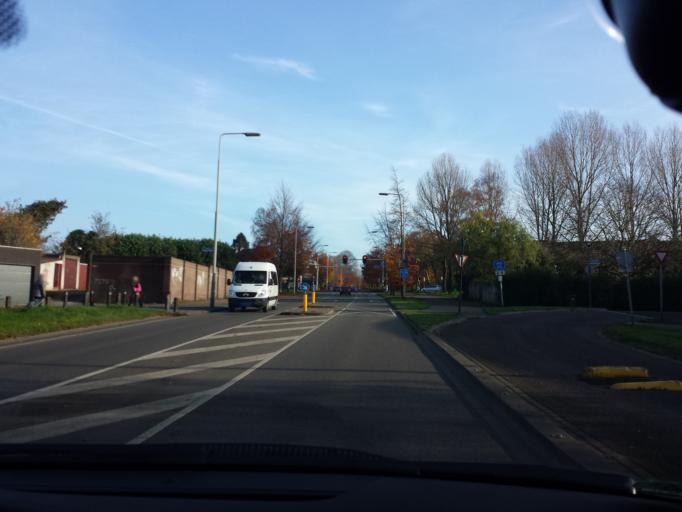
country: NL
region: Limburg
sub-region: Gemeente Kerkrade
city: Kerkrade
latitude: 50.8595
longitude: 6.0666
